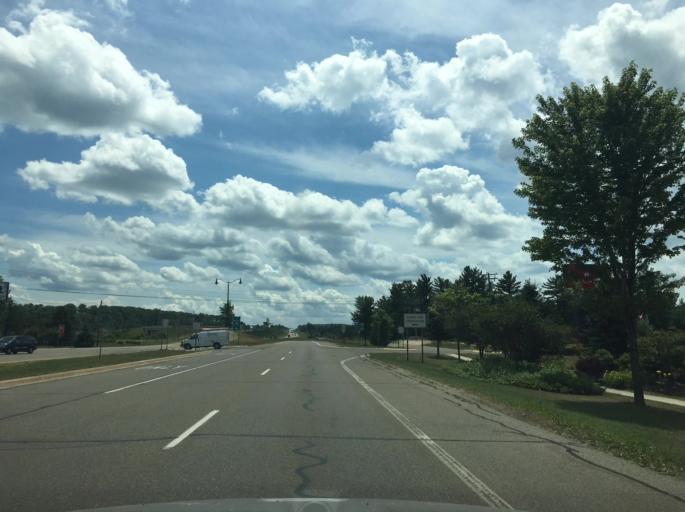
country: US
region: Michigan
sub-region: Crawford County
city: Grayling
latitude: 44.6478
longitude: -84.7088
